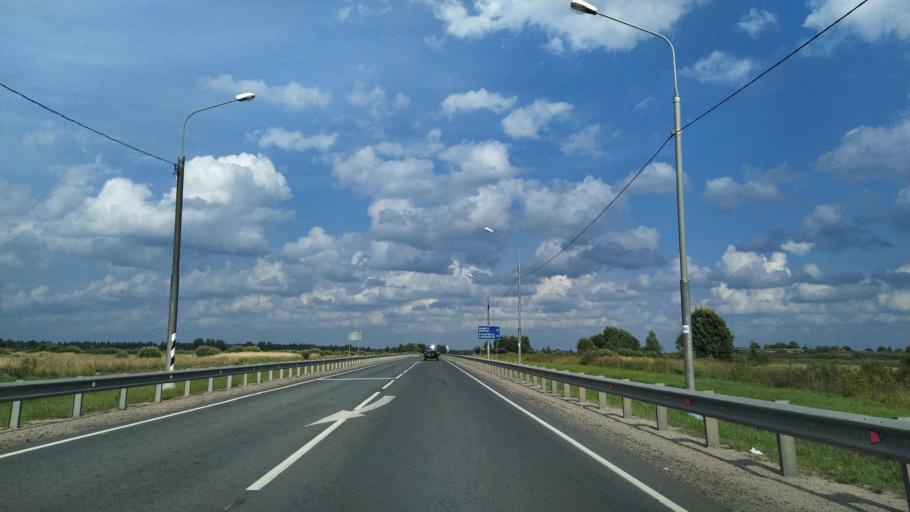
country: RU
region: Novgorod
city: Sol'tsy
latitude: 58.1298
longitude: 30.3629
